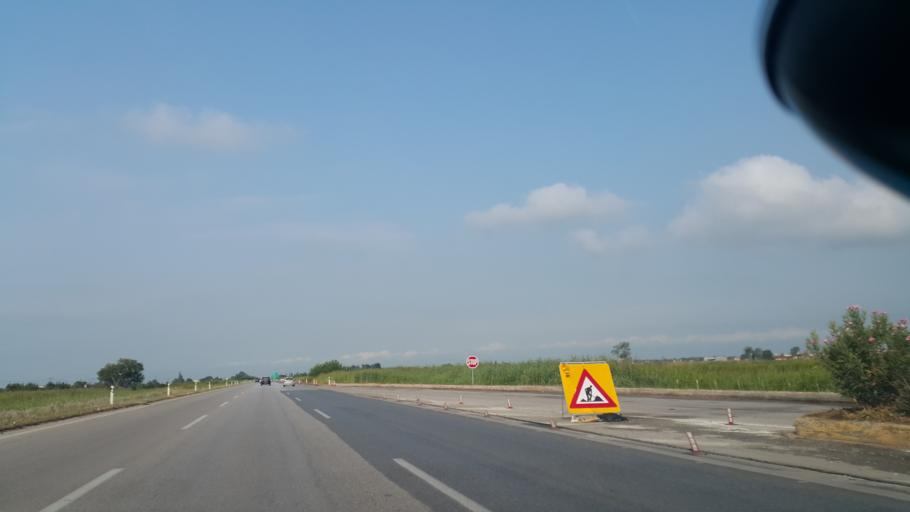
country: GR
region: Central Macedonia
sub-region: Nomos Thessalonikis
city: Chalastra
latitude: 40.6259
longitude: 22.7652
